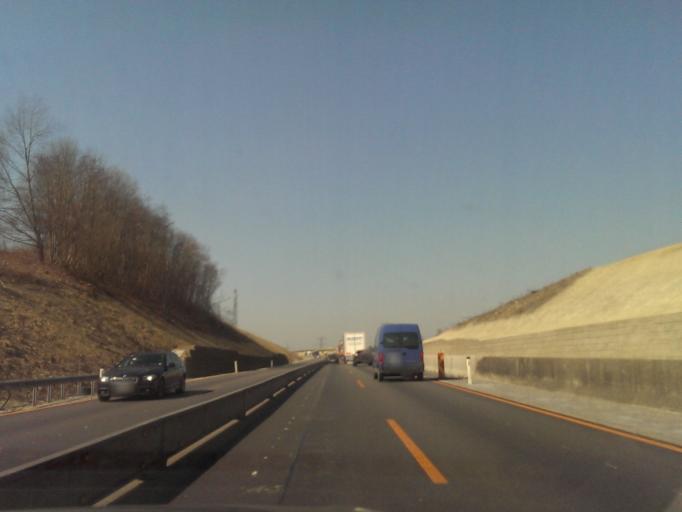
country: AT
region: Upper Austria
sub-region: Politischer Bezirk Vocklabruck
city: Wolfsegg am Hausruck
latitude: 48.1815
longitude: 13.6931
